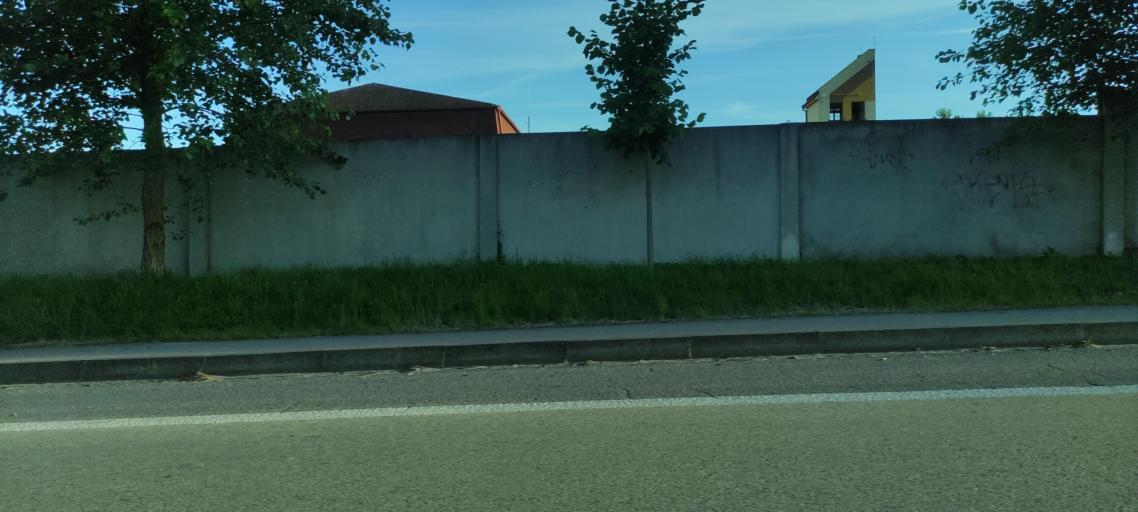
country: CZ
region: Jihocesky
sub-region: Okres Jindrichuv Hradec
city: Jindrichuv Hradec
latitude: 49.1510
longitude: 15.0132
